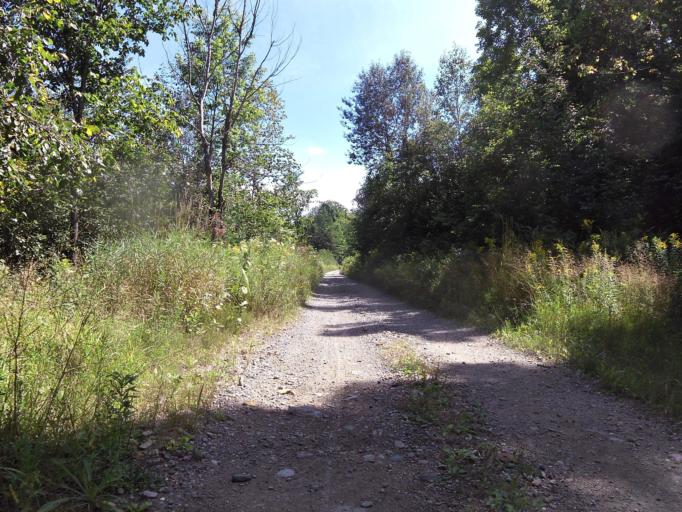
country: CA
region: Ontario
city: Renfrew
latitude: 45.0200
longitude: -76.7026
